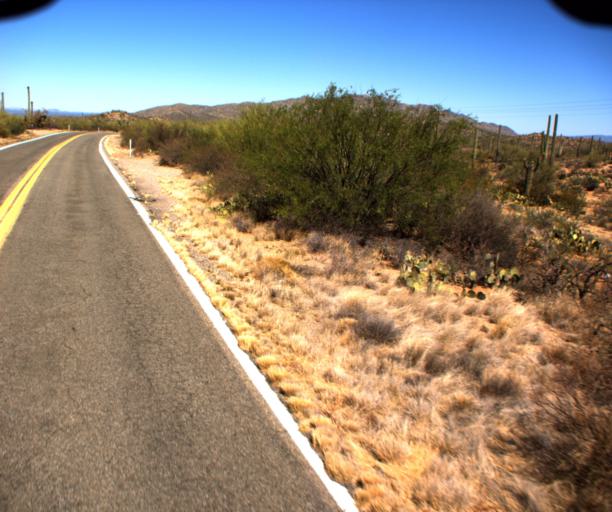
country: US
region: Arizona
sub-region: Pima County
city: Sells
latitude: 32.1756
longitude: -112.1872
